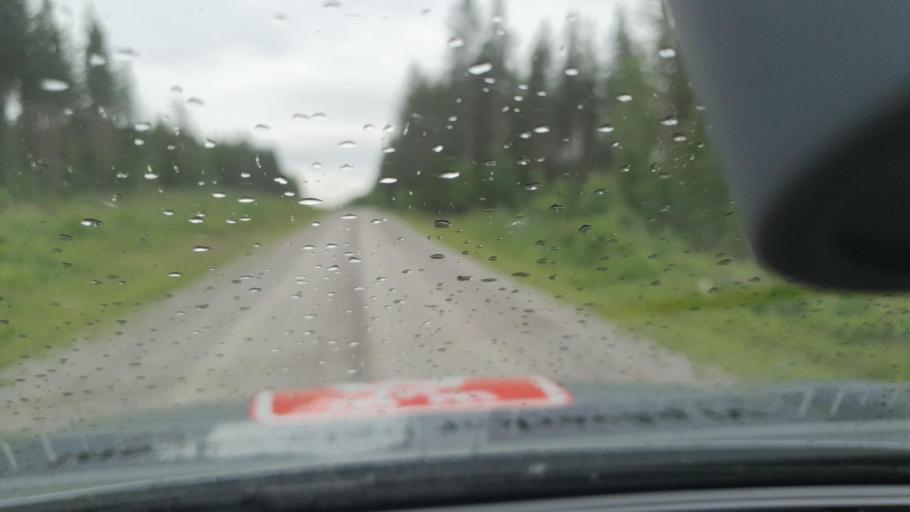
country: SE
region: Norrbotten
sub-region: Kalix Kommun
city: Rolfs
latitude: 66.0554
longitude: 23.0268
